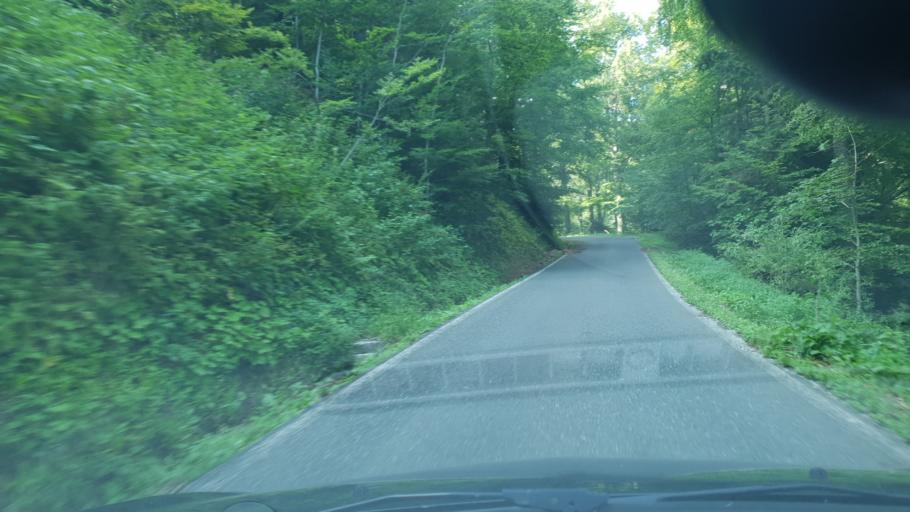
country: HR
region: Grad Zagreb
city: Kasina
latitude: 45.8952
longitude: 15.9540
